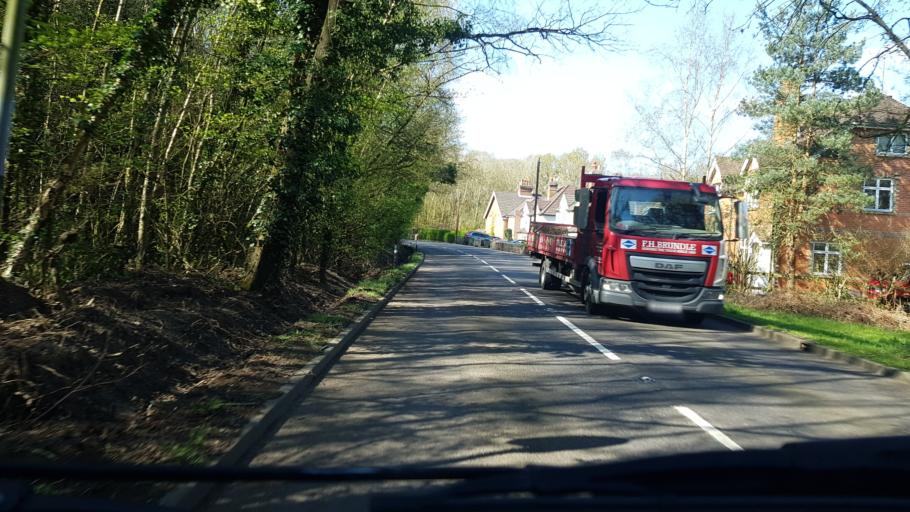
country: GB
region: England
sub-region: Surrey
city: Normandy
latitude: 51.2632
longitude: -0.6756
